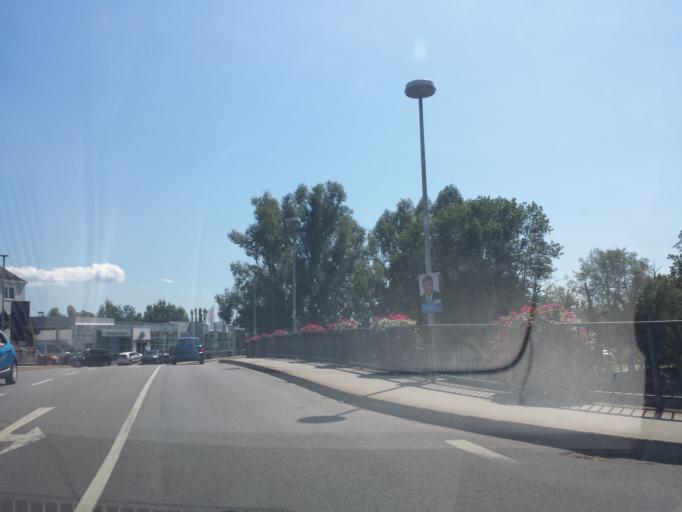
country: DE
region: Bavaria
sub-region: Upper Palatinate
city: Cham
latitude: 49.2166
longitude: 12.6676
